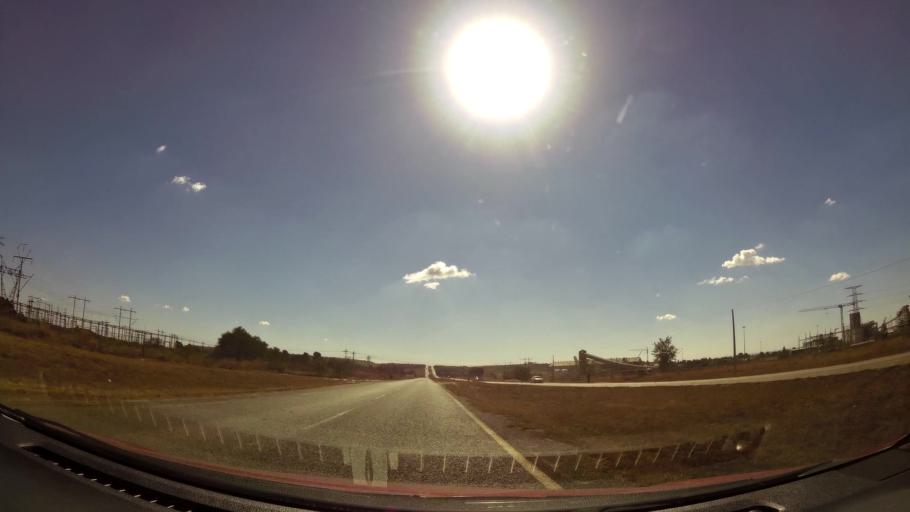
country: ZA
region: Gauteng
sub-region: West Rand District Municipality
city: Carletonville
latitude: -26.4052
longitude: 27.4273
